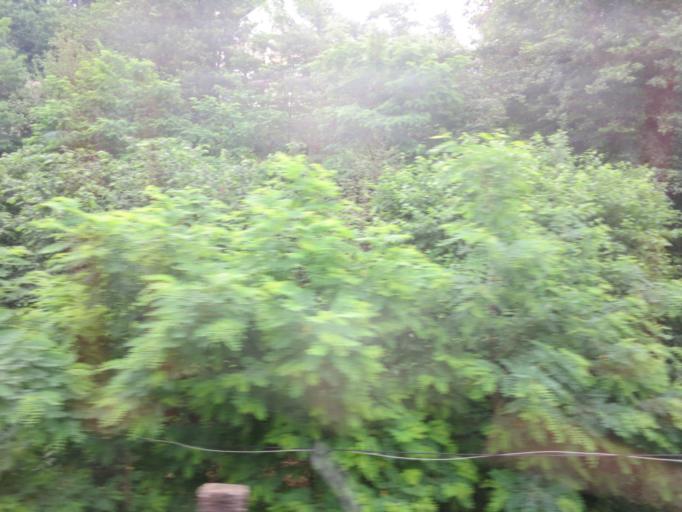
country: GE
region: Ajaria
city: Kobuleti
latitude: 41.7682
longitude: 41.7522
